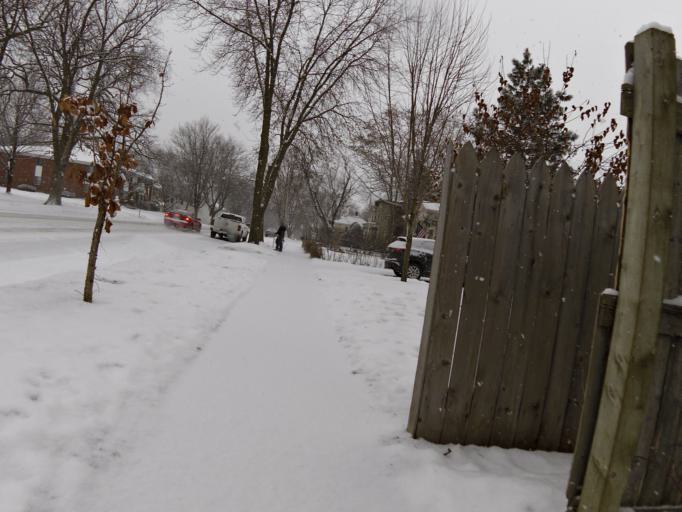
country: US
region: Wisconsin
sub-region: Saint Croix County
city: Hudson
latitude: 44.9786
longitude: -92.7557
